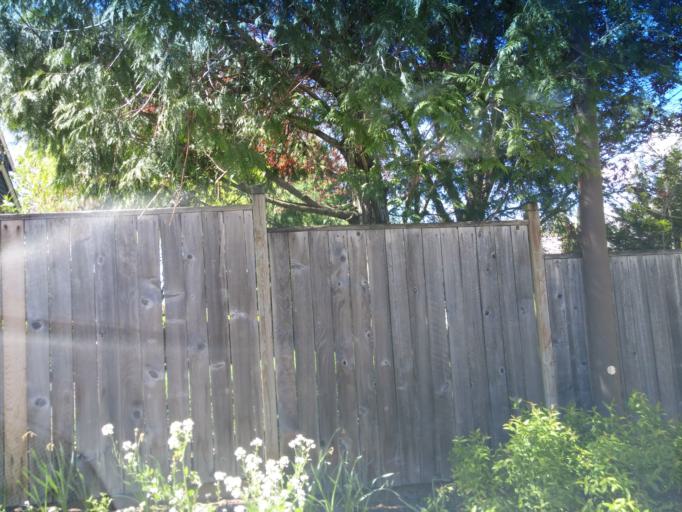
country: US
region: Oregon
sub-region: Washington County
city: West Haven
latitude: 45.5303
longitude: -122.7782
